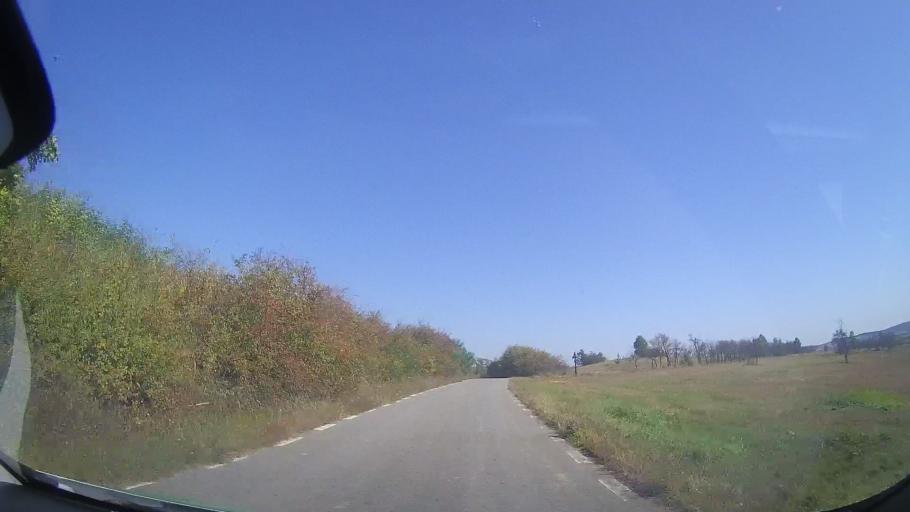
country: RO
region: Timis
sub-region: Comuna Ohaba Lunga
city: Ohaba Lunga
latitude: 45.9145
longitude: 21.9514
